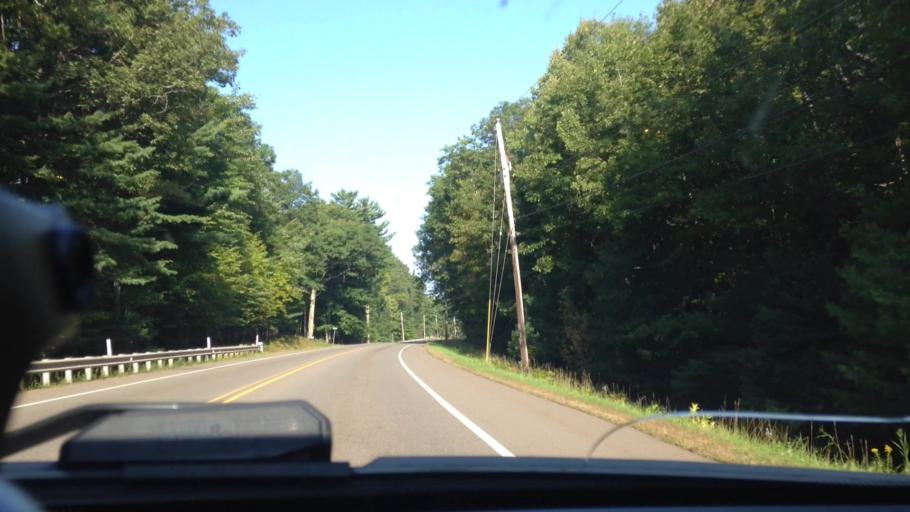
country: US
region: Michigan
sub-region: Dickinson County
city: Quinnesec
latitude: 45.8325
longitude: -88.0045
